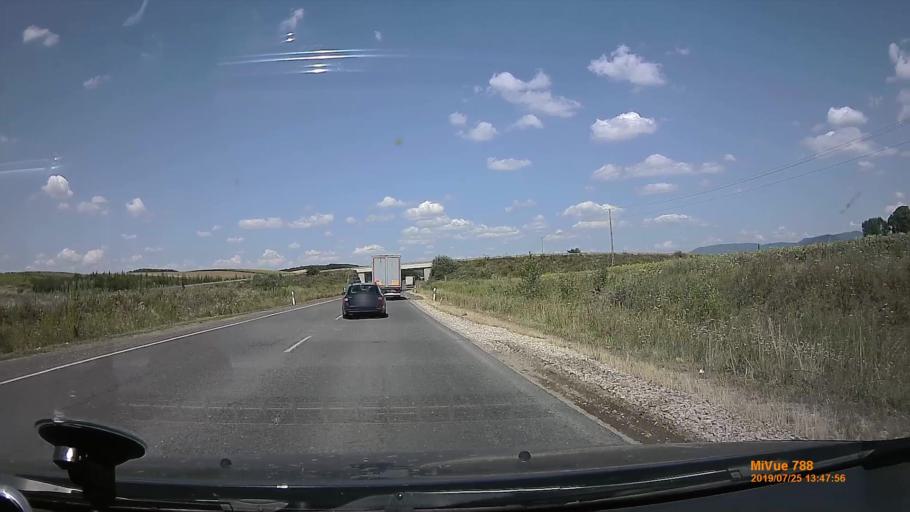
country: HU
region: Borsod-Abauj-Zemplen
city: Gonc
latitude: 48.5018
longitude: 21.2213
